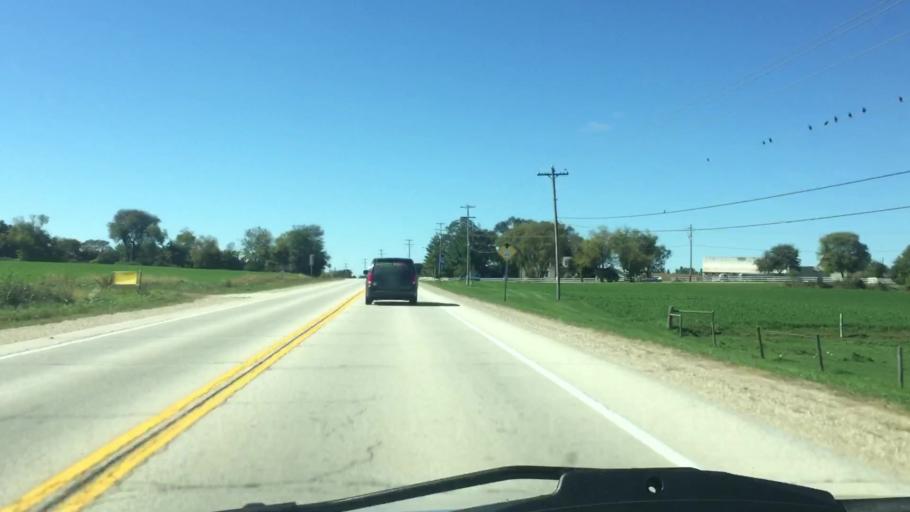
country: US
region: Wisconsin
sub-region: Waukesha County
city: Wales
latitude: 43.0196
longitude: -88.3618
